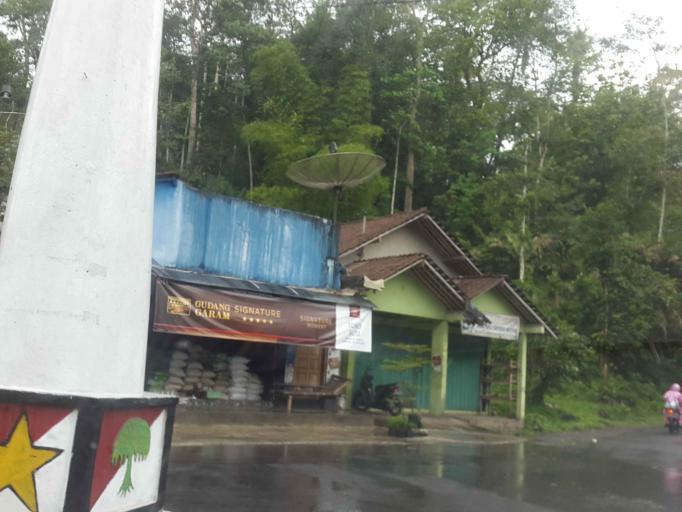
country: ID
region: Central Java
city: Mertoyudan
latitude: -7.4966
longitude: 110.2727
